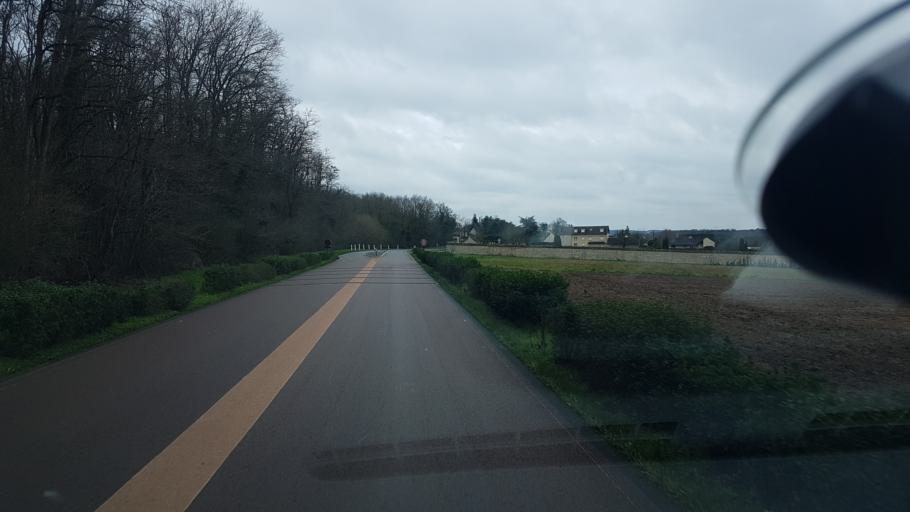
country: FR
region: Ile-de-France
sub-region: Departement de Seine-et-Marne
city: Montcourt-Fromonville
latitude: 48.2748
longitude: 2.7468
